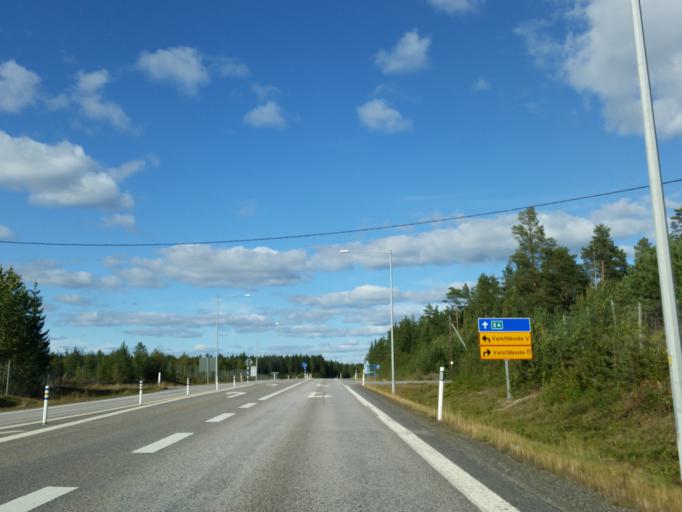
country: SE
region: Vaesterbotten
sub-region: Robertsfors Kommun
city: Robertsfors
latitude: 64.1171
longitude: 20.8814
